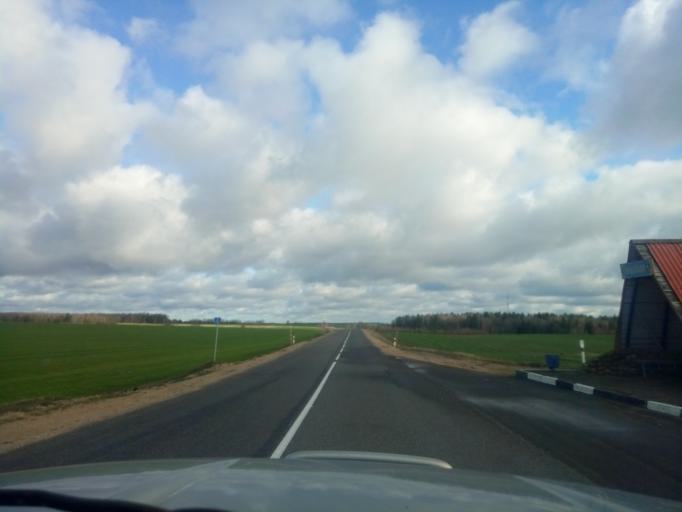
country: BY
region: Minsk
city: Kapyl'
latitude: 53.1435
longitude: 27.0304
